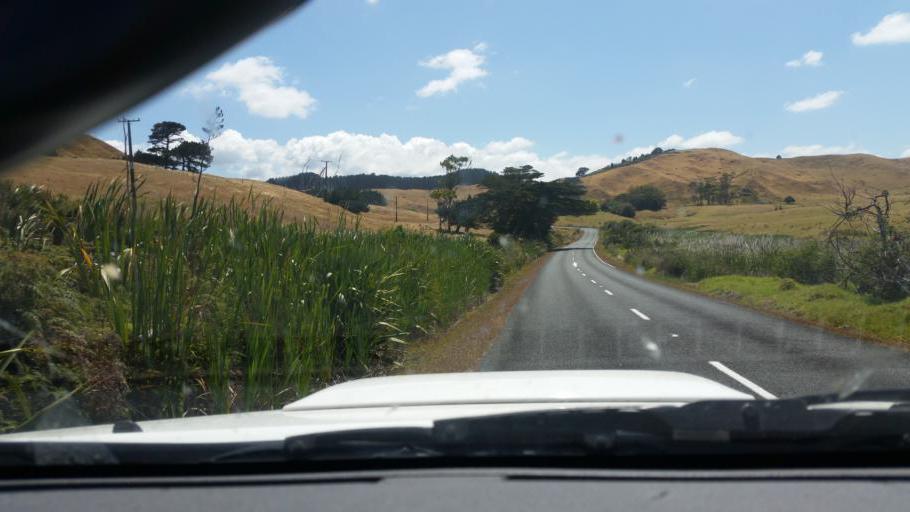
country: NZ
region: Northland
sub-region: Kaipara District
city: Dargaville
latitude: -35.8264
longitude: 173.6746
